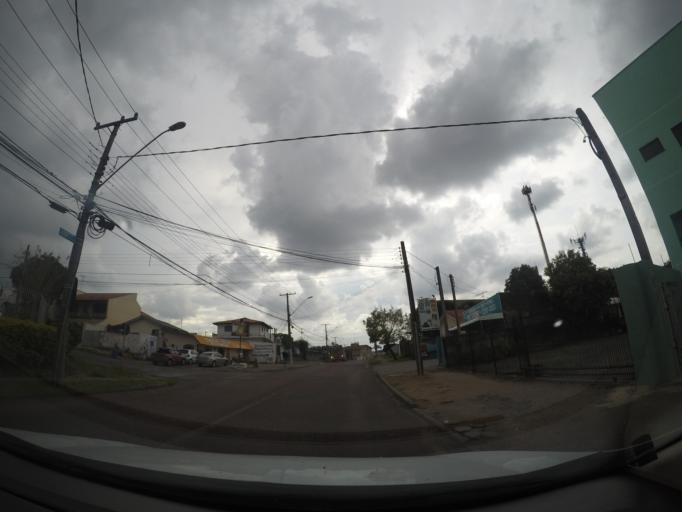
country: BR
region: Parana
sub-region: Sao Jose Dos Pinhais
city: Sao Jose dos Pinhais
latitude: -25.5325
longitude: -49.2439
